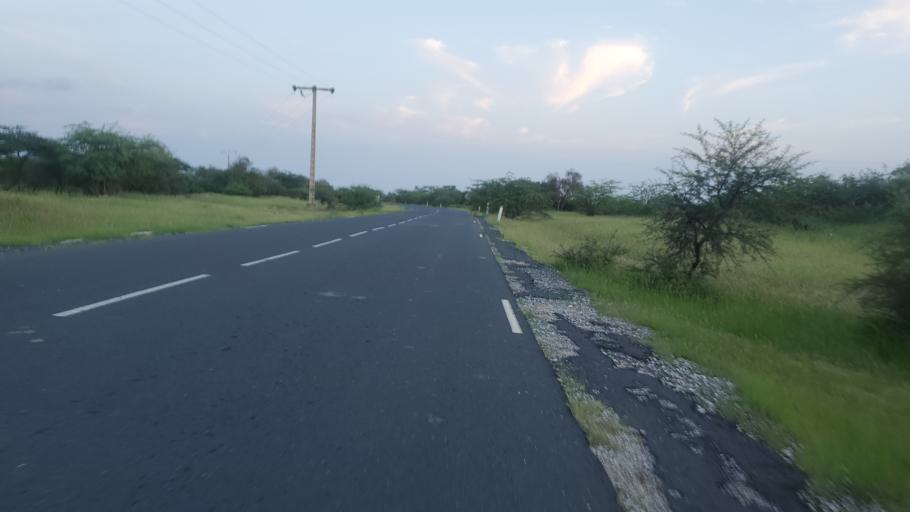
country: SN
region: Saint-Louis
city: Saint-Louis
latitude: 16.1041
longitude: -16.4116
